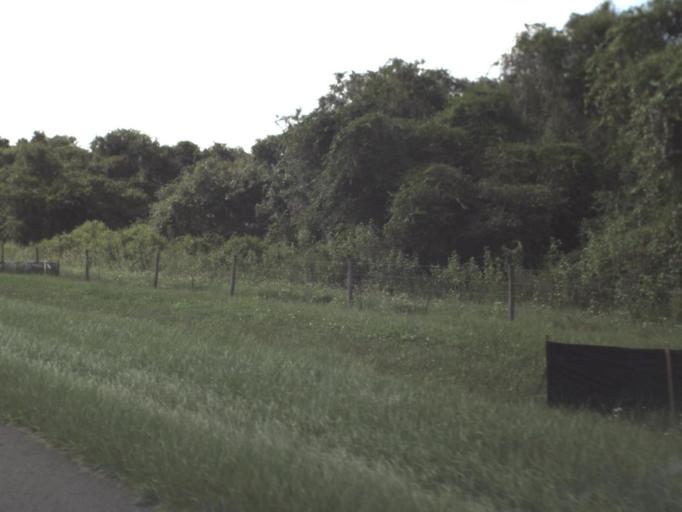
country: US
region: Florida
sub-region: Sarasota County
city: The Meadows
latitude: 27.4747
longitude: -82.3141
